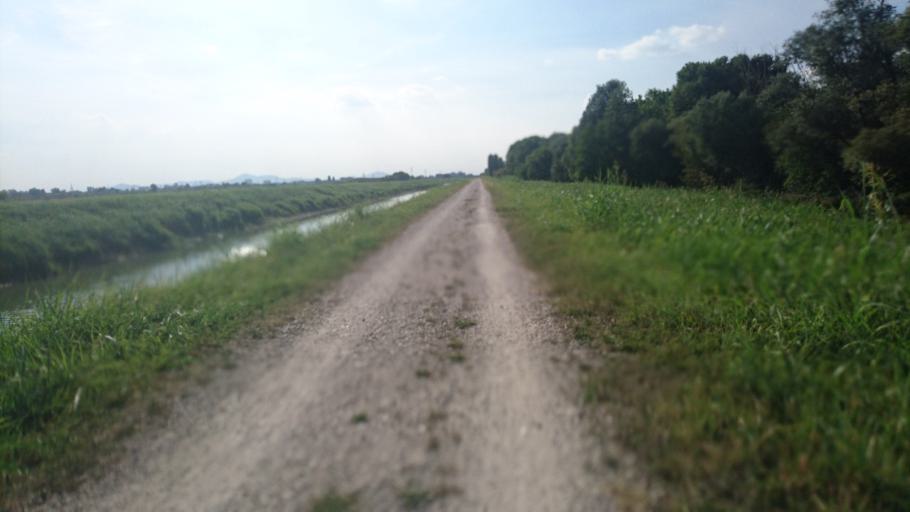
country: IT
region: Veneto
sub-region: Provincia di Venezia
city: Tombelle
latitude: 45.4082
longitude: 11.9854
